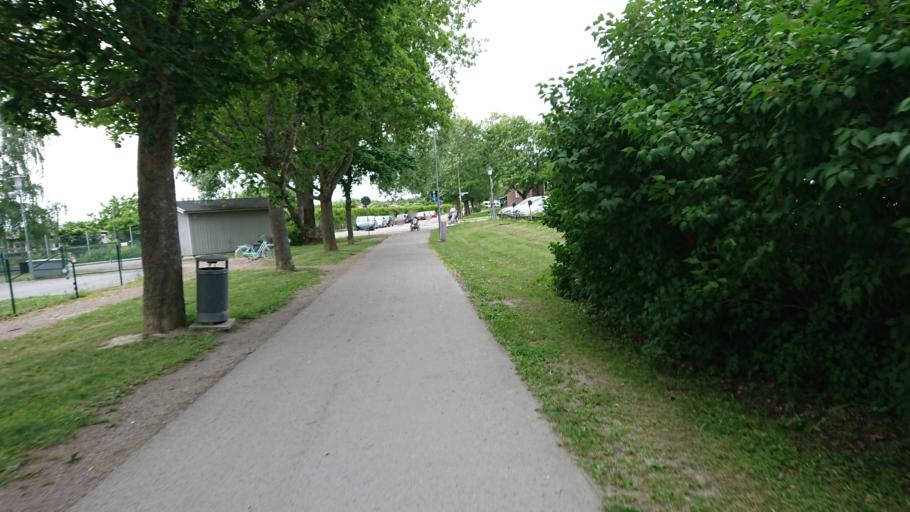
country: SE
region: Uppsala
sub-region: Uppsala Kommun
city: Uppsala
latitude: 59.8741
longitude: 17.6170
